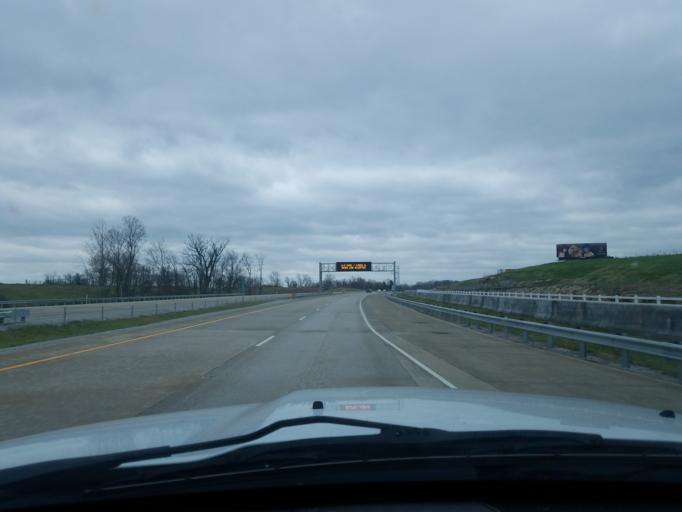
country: US
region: Kentucky
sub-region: Jefferson County
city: Prospect
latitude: 38.3498
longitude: -85.6584
